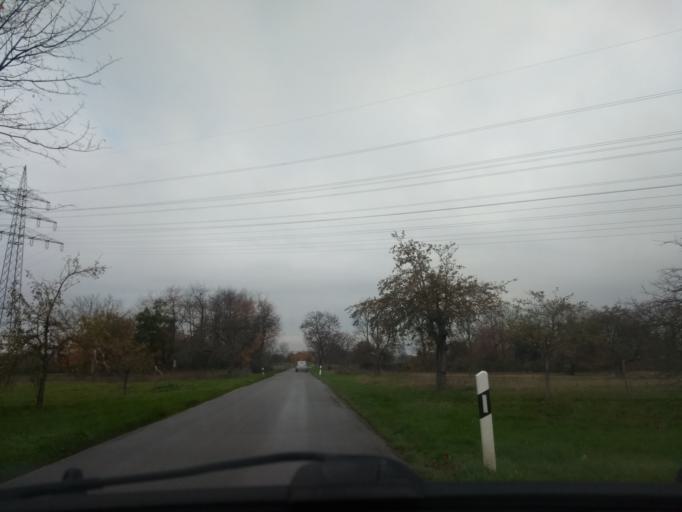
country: DE
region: Baden-Wuerttemberg
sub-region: Karlsruhe Region
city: Kuppenheim
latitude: 48.8484
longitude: 8.2598
